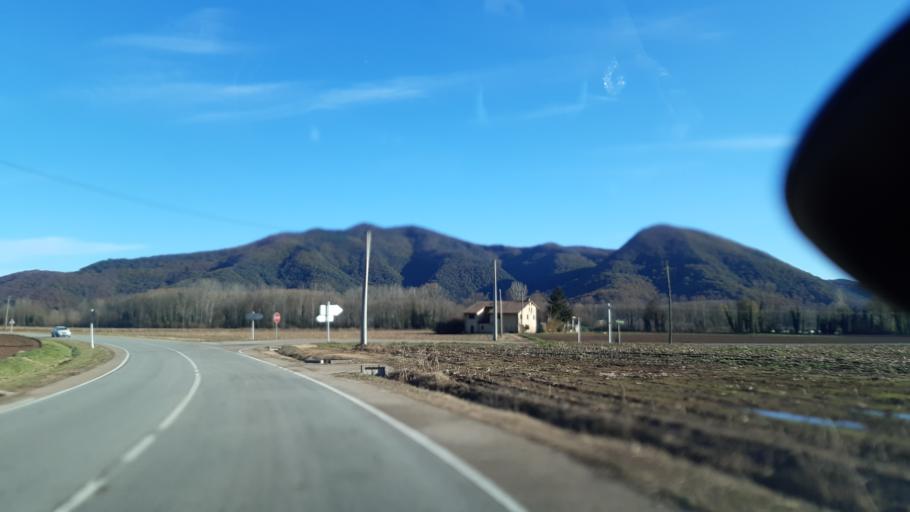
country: ES
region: Catalonia
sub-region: Provincia de Girona
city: Bas
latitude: 42.1466
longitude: 2.4406
